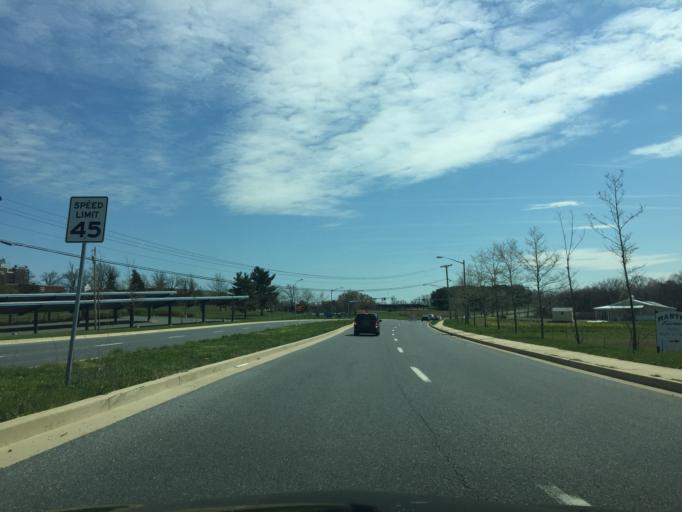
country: US
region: Maryland
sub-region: Baltimore County
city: Rossville
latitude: 39.3555
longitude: -76.4858
